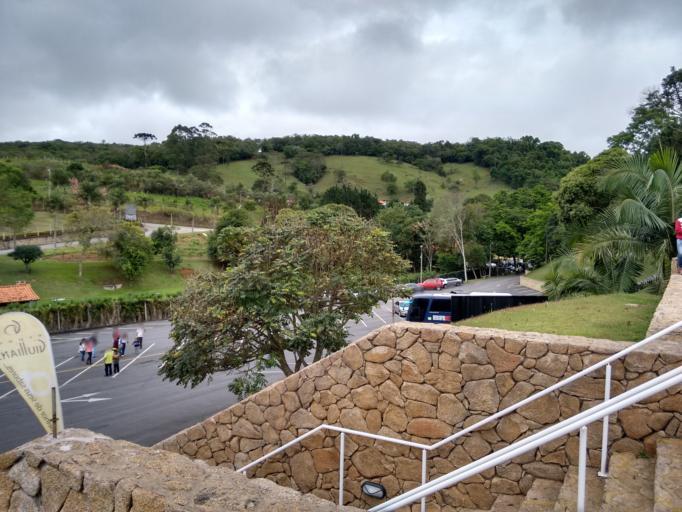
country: BR
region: Sao Paulo
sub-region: Mairinque
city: Mairinque
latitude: -23.6099
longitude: -47.1589
